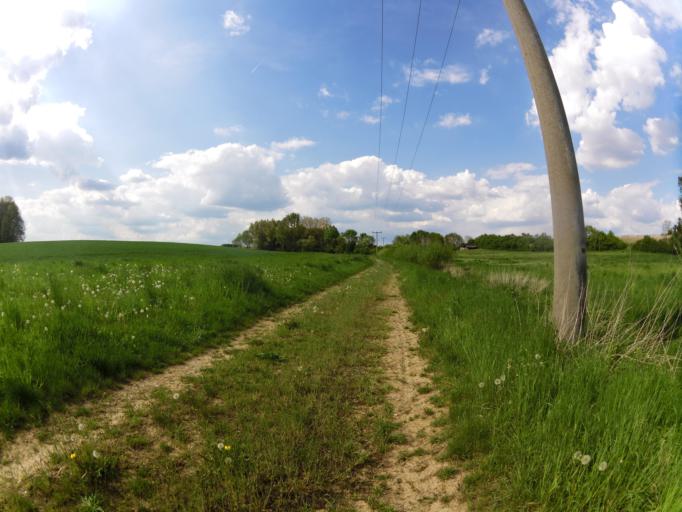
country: DE
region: Bavaria
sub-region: Regierungsbezirk Unterfranken
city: Giebelstadt
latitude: 49.6249
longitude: 9.9444
